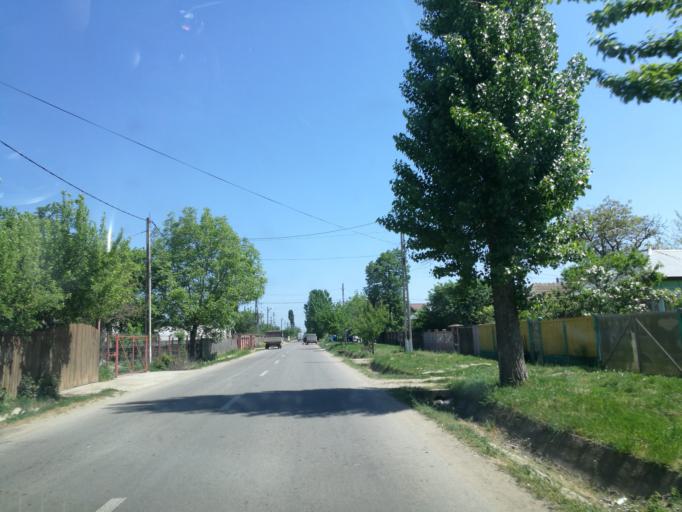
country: RO
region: Ialomita
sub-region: Comuna Maia
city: Maia
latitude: 44.7409
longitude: 26.4029
